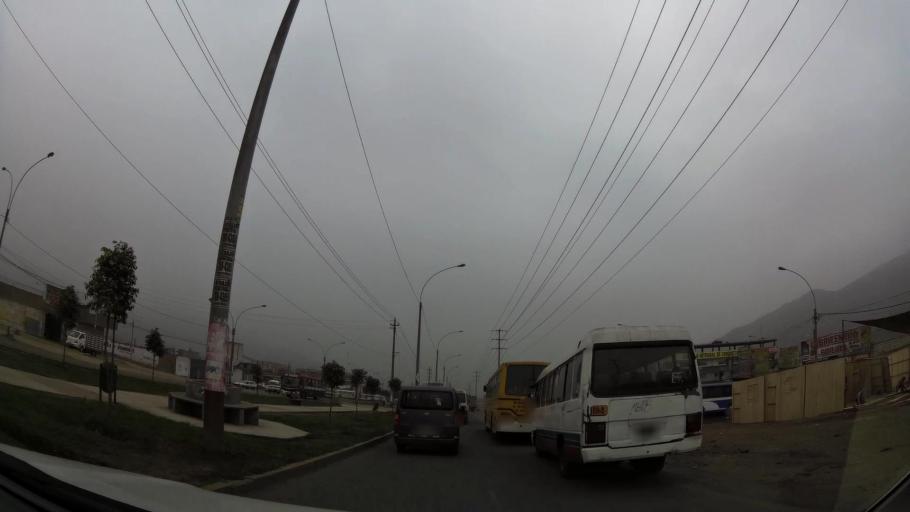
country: PE
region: Lima
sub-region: Lima
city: Urb. Santo Domingo
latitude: -11.9269
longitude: -76.9645
